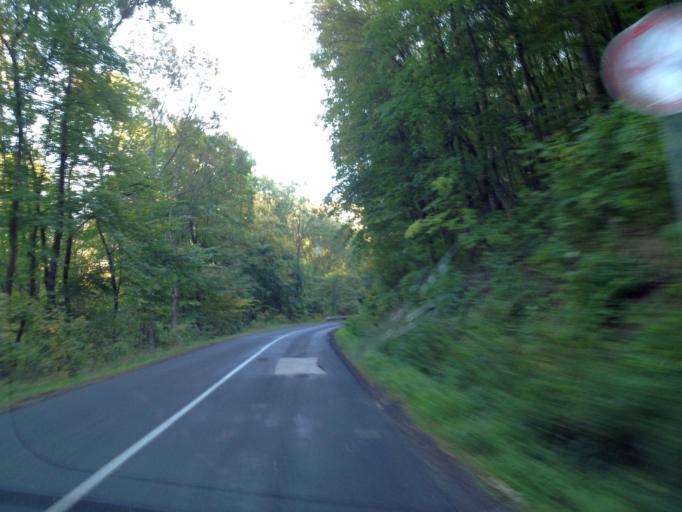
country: HU
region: Komarom-Esztergom
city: Kesztolc
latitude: 47.7223
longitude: 18.8438
